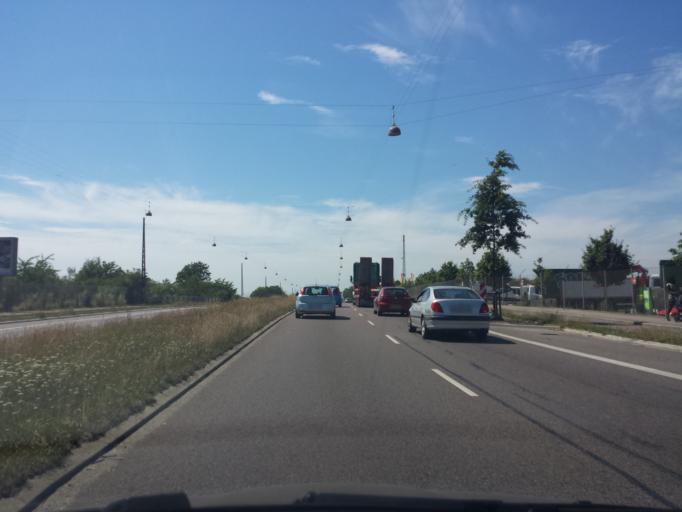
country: DK
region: Capital Region
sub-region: Frederiksberg Kommune
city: Frederiksberg
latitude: 55.6503
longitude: 12.5202
